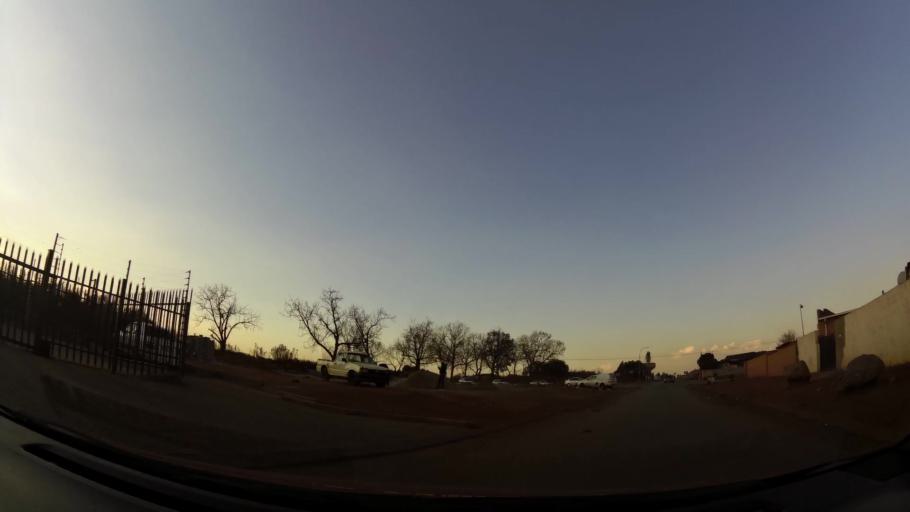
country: ZA
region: Gauteng
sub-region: City of Johannesburg Metropolitan Municipality
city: Soweto
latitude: -26.2186
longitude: 27.8567
